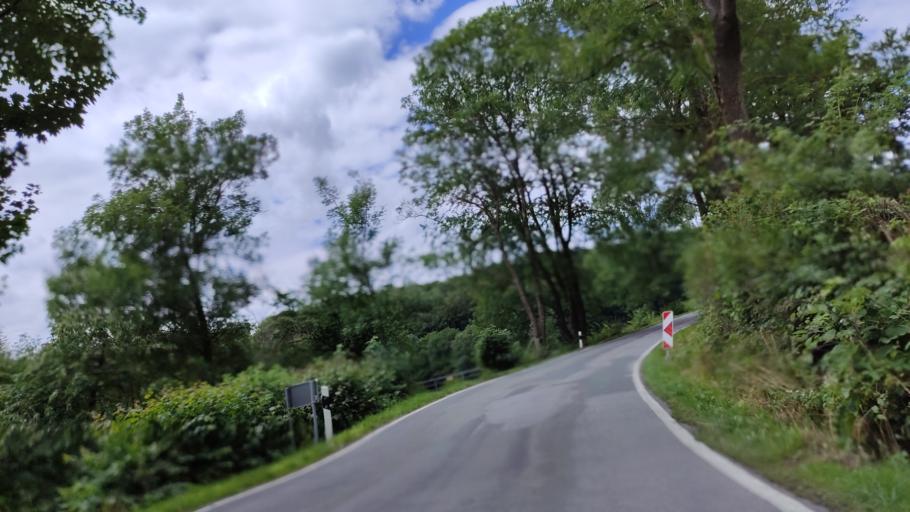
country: DE
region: North Rhine-Westphalia
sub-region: Regierungsbezirk Detmold
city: Nieheim
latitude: 51.7587
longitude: 9.0763
